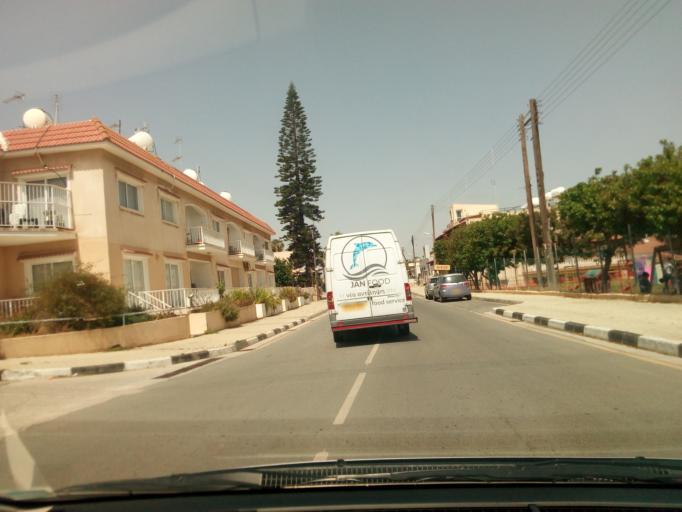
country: CY
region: Larnaka
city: Xylotymbou
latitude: 34.9895
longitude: 33.7801
